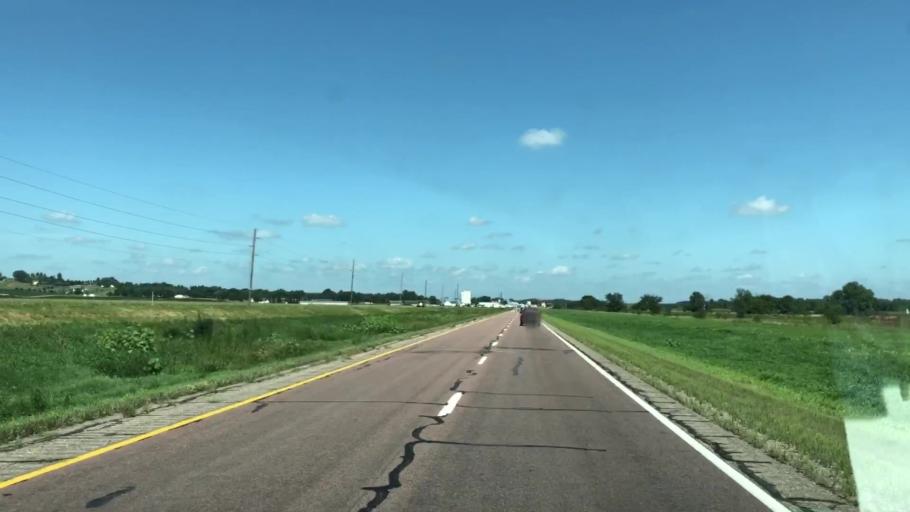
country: US
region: Iowa
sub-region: Plymouth County
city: Le Mars
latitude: 42.7044
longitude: -96.2555
